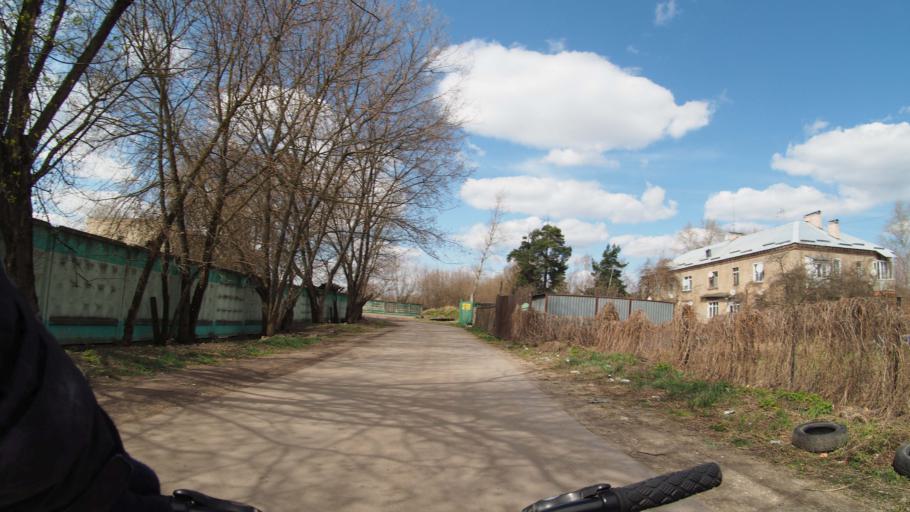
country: RU
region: Moskovskaya
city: Ramenskoye
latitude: 55.5565
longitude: 38.2549
